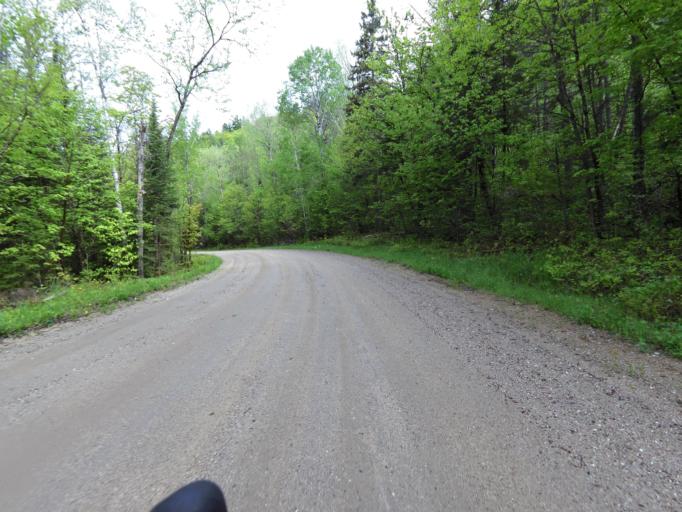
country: CA
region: Quebec
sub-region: Outaouais
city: Wakefield
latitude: 45.7583
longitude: -75.9075
